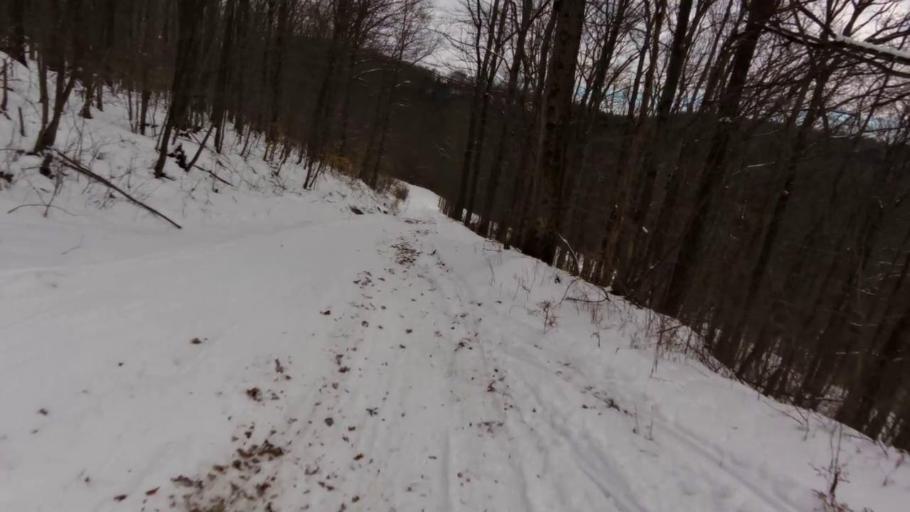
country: US
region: Pennsylvania
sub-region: McKean County
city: Foster Brook
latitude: 42.0083
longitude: -78.6048
